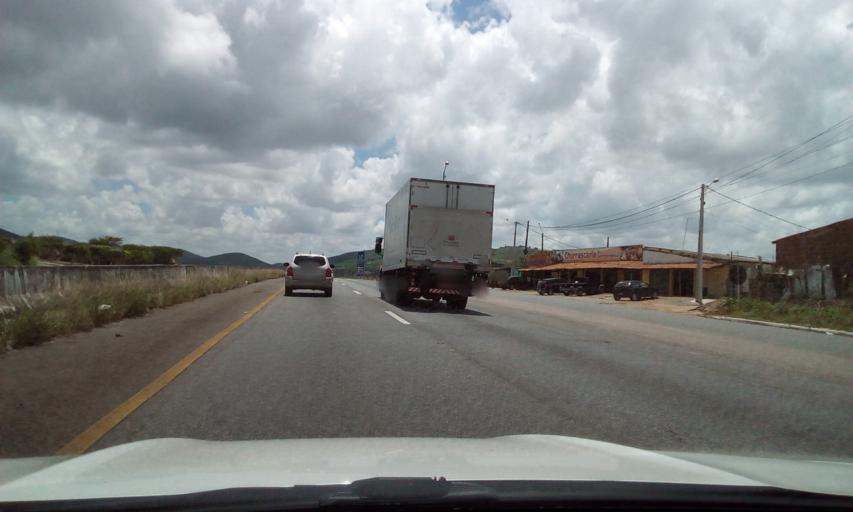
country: BR
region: Pernambuco
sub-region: Pombos
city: Pombos
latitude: -8.1476
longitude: -35.4055
